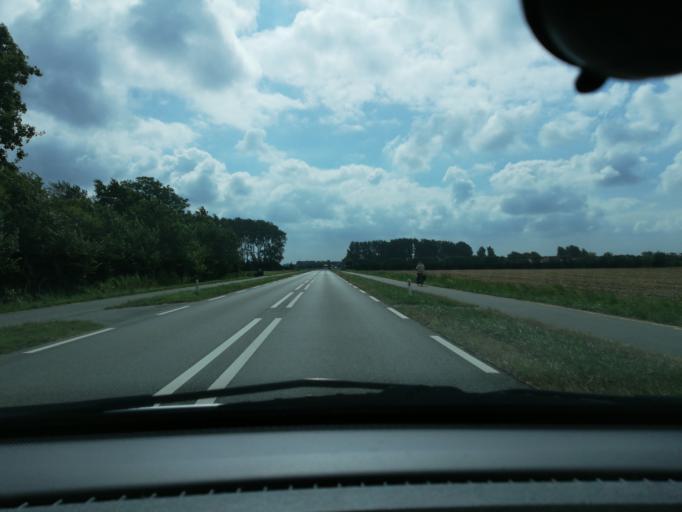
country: NL
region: Zeeland
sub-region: Gemeente Middelburg
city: Middelburg
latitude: 51.5655
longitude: 3.5731
